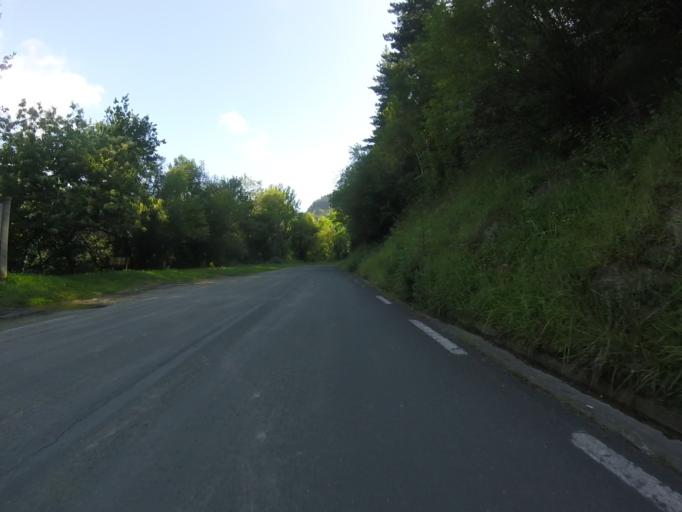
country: ES
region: Basque Country
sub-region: Provincia de Guipuzcoa
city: Ormaiztegui
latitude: 43.0695
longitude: -2.2379
